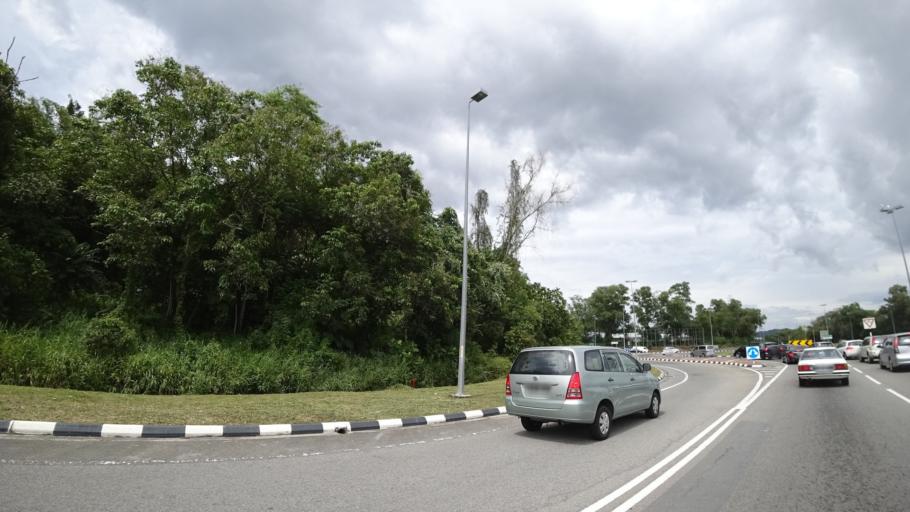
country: BN
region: Brunei and Muara
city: Bandar Seri Begawan
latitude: 4.8960
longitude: 114.9104
